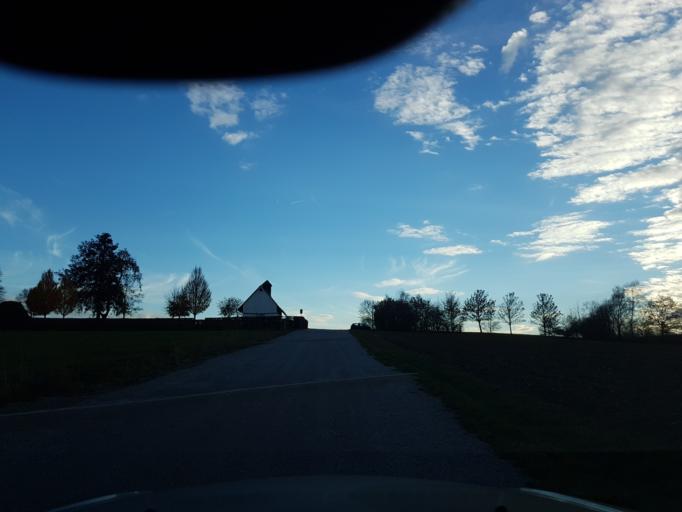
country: DE
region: Hesse
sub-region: Regierungsbezirk Darmstadt
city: Bad Schwalbach
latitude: 50.1220
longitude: 8.0175
